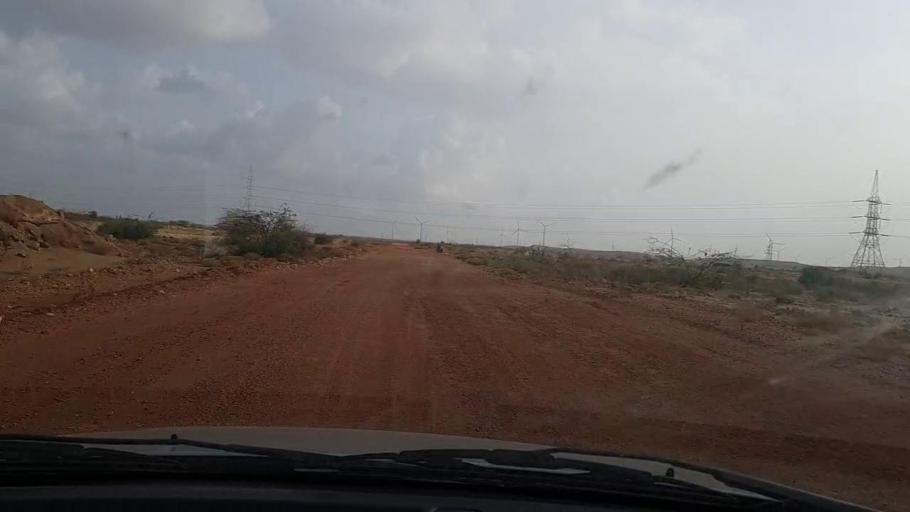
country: PK
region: Sindh
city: Thatta
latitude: 25.0612
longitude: 67.8840
